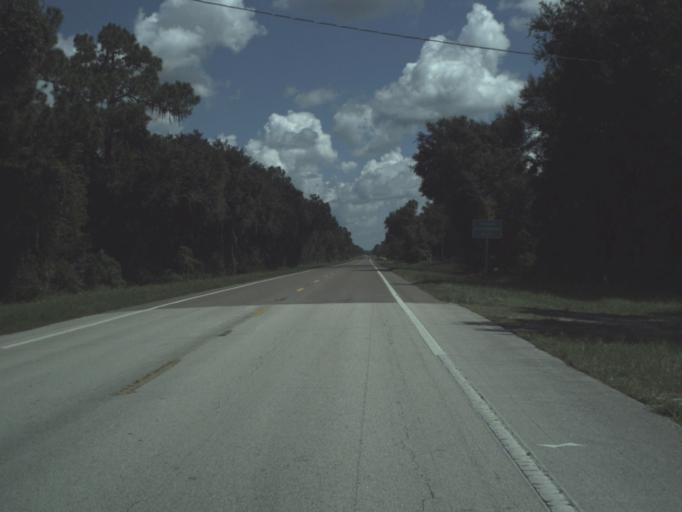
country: US
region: Florida
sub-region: Hillsborough County
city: Sun City Center
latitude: 27.6462
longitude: -82.3851
